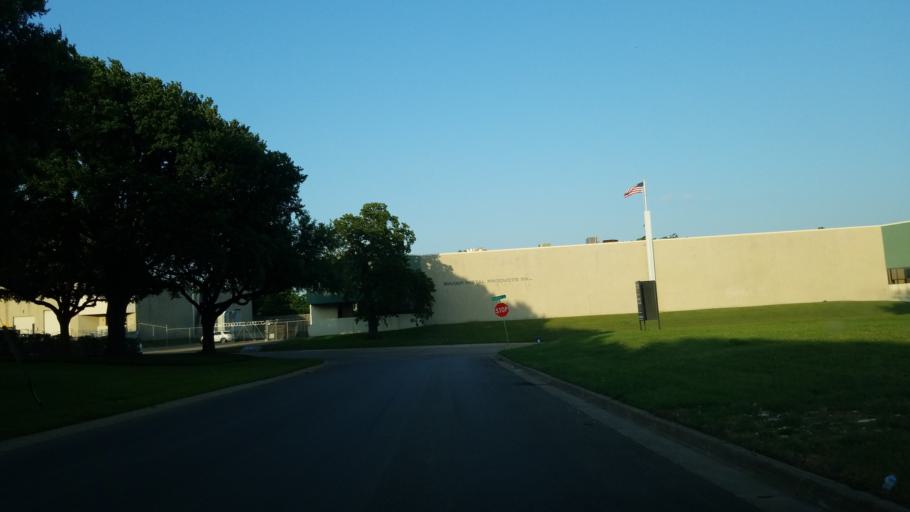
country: US
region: Texas
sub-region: Dallas County
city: Farmers Branch
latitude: 32.8890
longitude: -96.8837
